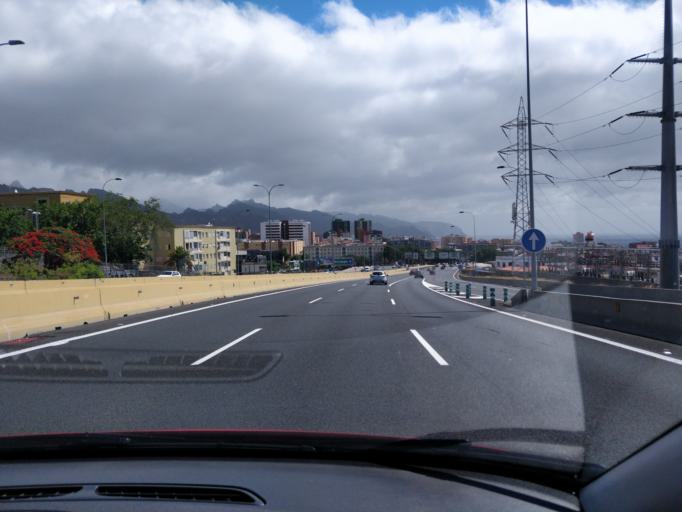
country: ES
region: Canary Islands
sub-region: Provincia de Santa Cruz de Tenerife
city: Santa Cruz de Tenerife
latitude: 28.4545
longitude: -16.2702
